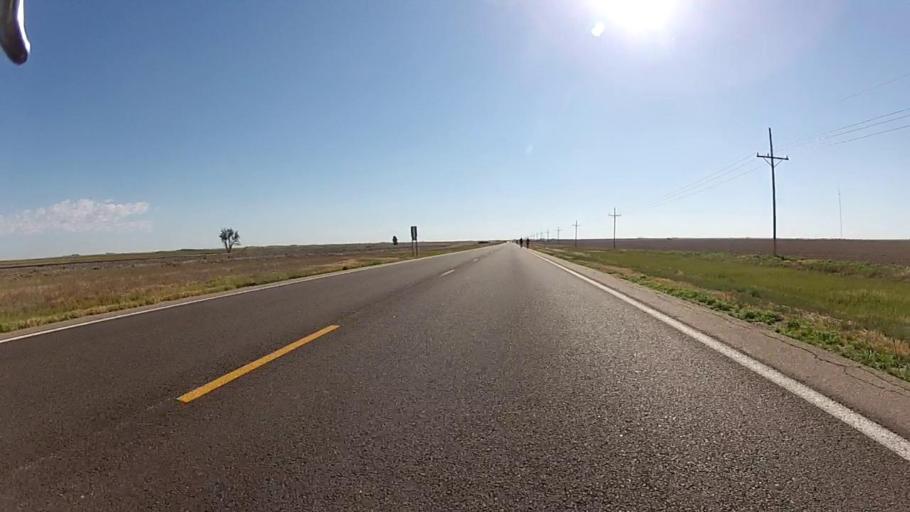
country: US
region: Kansas
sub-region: Haskell County
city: Sublette
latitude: 37.5597
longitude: -100.5710
